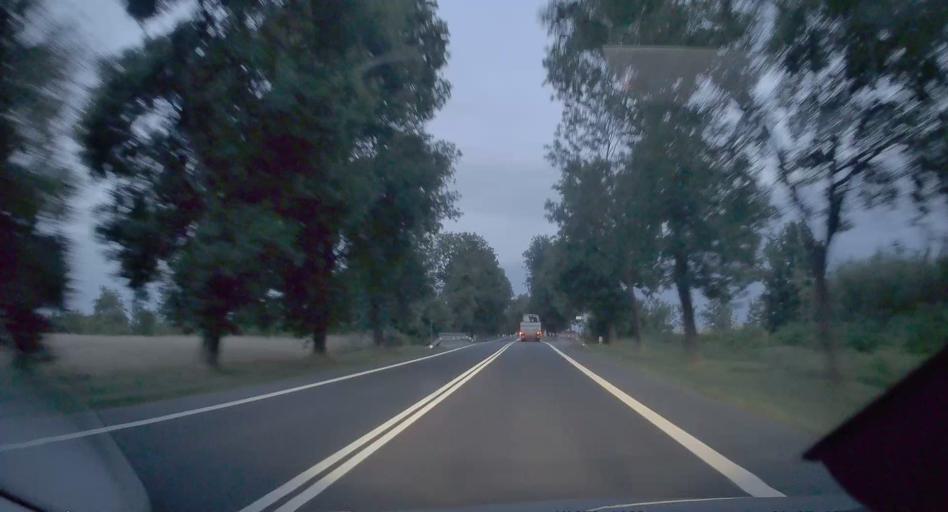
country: PL
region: Silesian Voivodeship
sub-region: Powiat klobucki
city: Klobuck
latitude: 50.9168
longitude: 18.8895
